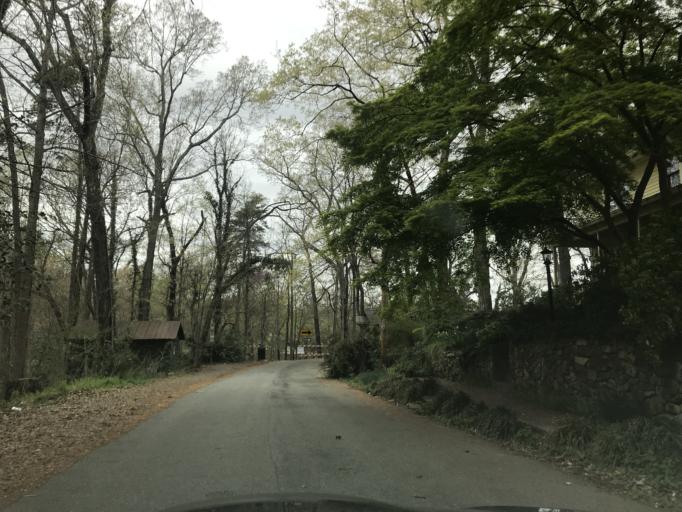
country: US
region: North Carolina
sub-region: Orange County
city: Chapel Hill
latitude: 35.9172
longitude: -79.0549
